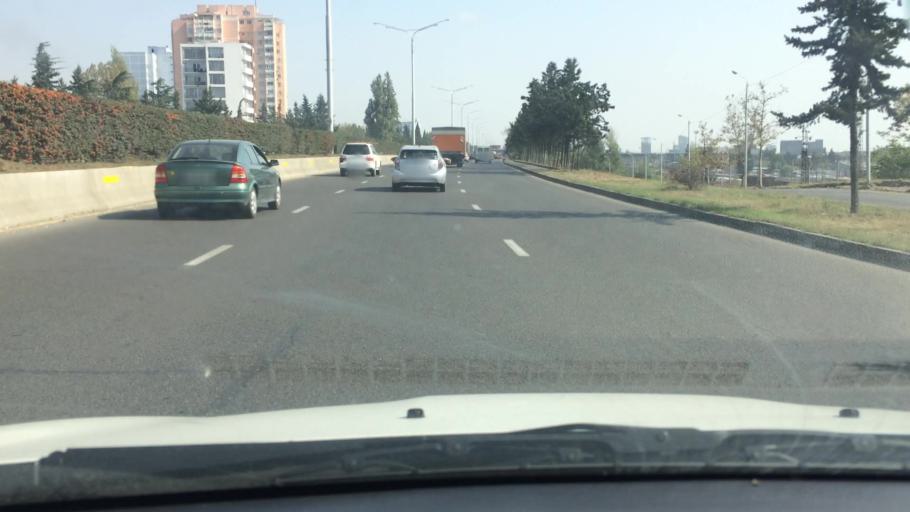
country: GE
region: T'bilisi
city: Tbilisi
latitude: 41.6872
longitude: 44.8506
